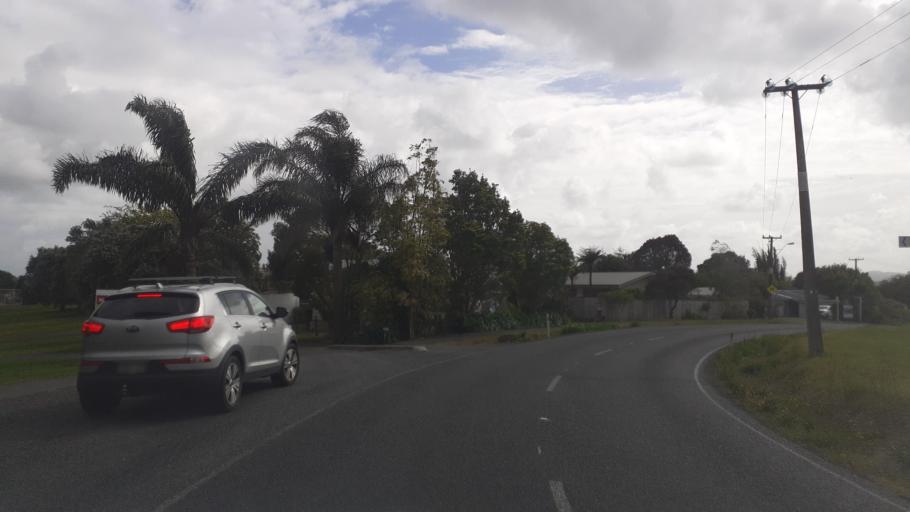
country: NZ
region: Northland
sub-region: Far North District
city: Kerikeri
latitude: -35.2180
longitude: 173.9789
